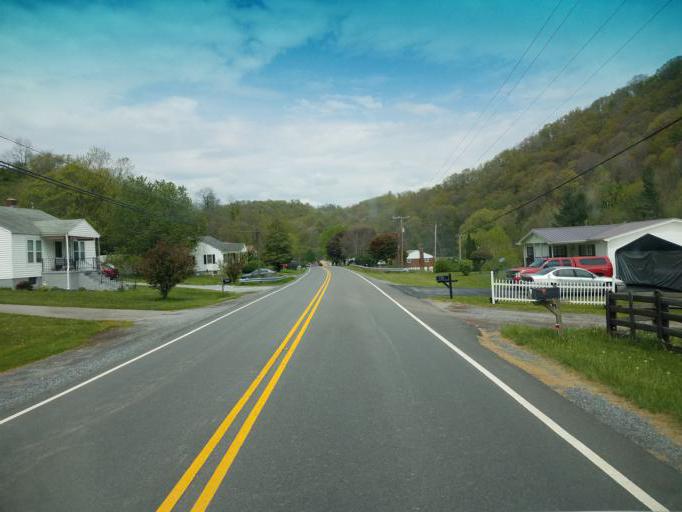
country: US
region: Virginia
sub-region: Smyth County
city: Marion
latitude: 36.8198
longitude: -81.4708
